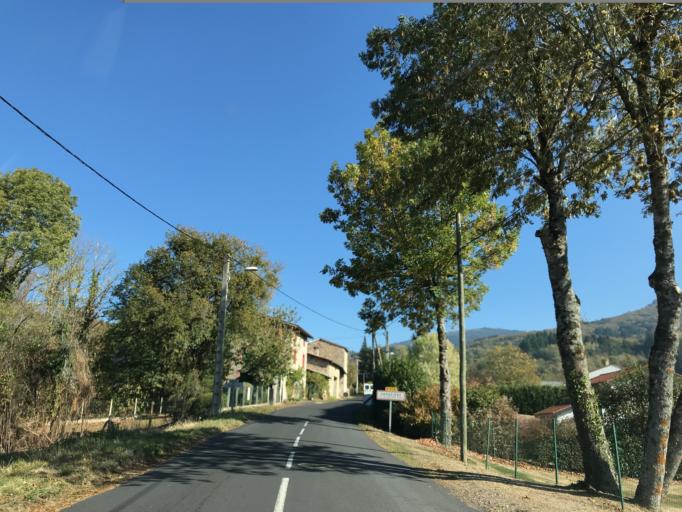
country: FR
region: Auvergne
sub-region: Departement du Puy-de-Dome
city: Escoutoux
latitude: 45.7955
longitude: 3.6075
